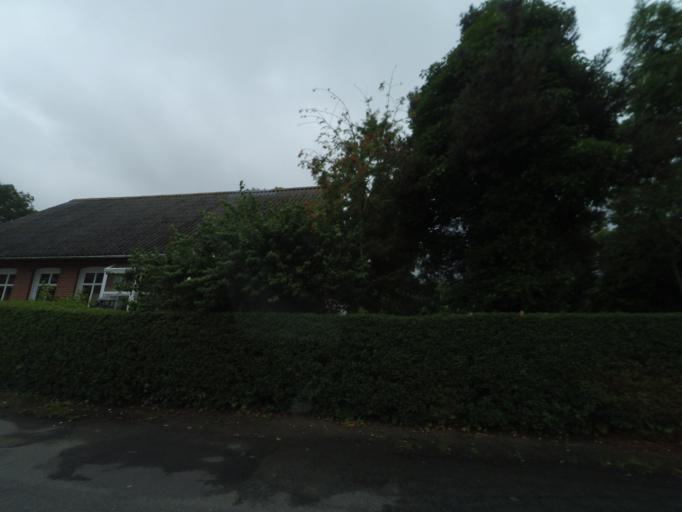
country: DK
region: South Denmark
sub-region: Nordfyns Kommune
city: Otterup
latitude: 55.5732
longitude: 10.3981
